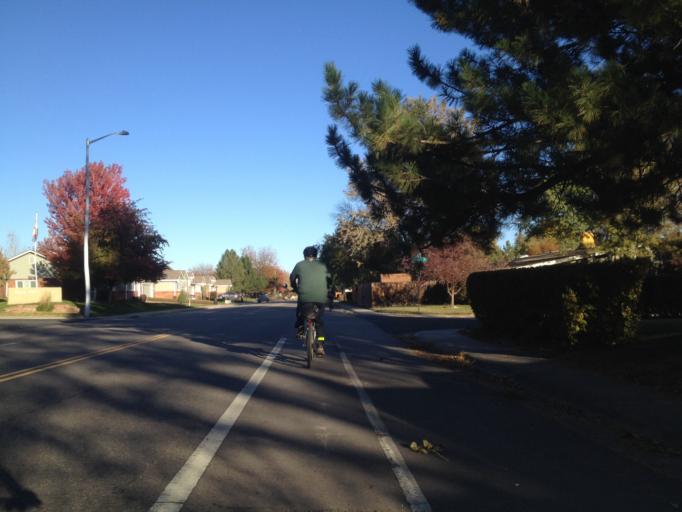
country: US
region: Colorado
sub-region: Boulder County
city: Longmont
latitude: 40.1849
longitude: -105.1262
